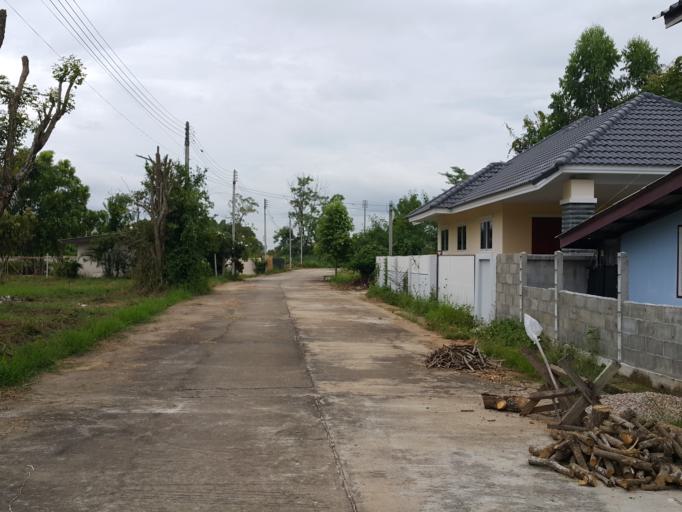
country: TH
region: Chiang Mai
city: San Sai
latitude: 18.8564
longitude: 99.1183
